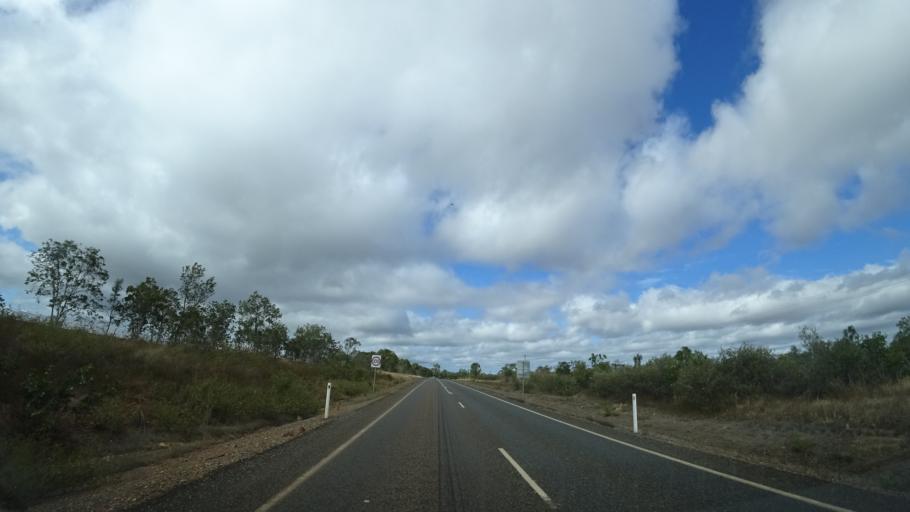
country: AU
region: Queensland
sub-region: Cook
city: Cooktown
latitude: -15.8694
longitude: 144.8599
